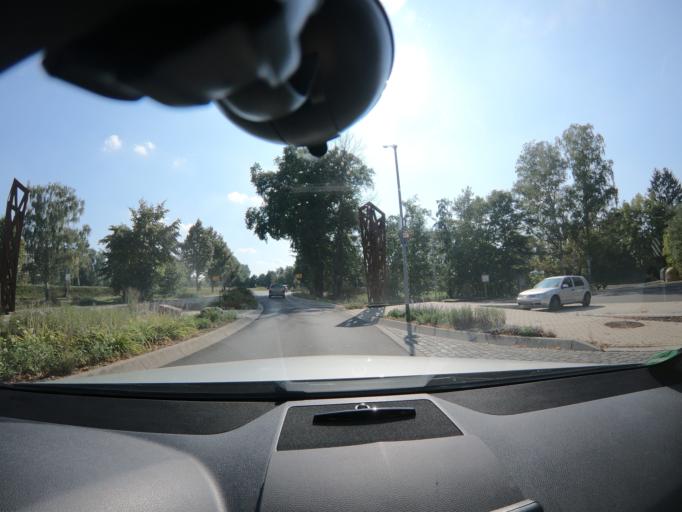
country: DE
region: Hesse
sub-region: Regierungsbezirk Giessen
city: Kirchhain
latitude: 50.8179
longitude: 8.9170
